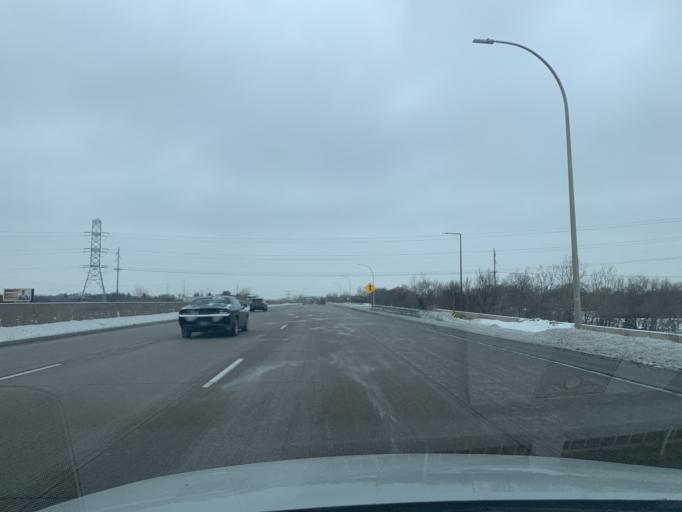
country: US
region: Minnesota
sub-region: Anoka County
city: Coon Rapids
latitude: 45.1408
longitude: -93.2856
